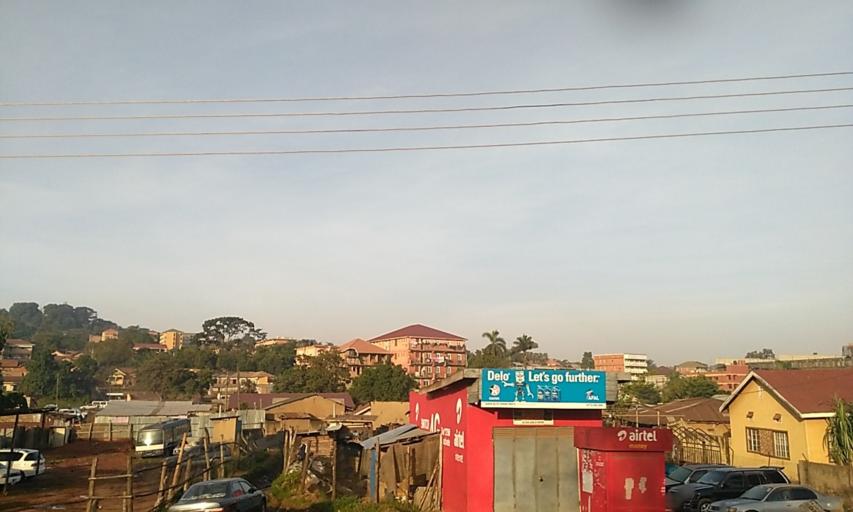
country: UG
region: Central Region
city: Kampala Central Division
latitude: 0.3443
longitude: 32.5712
